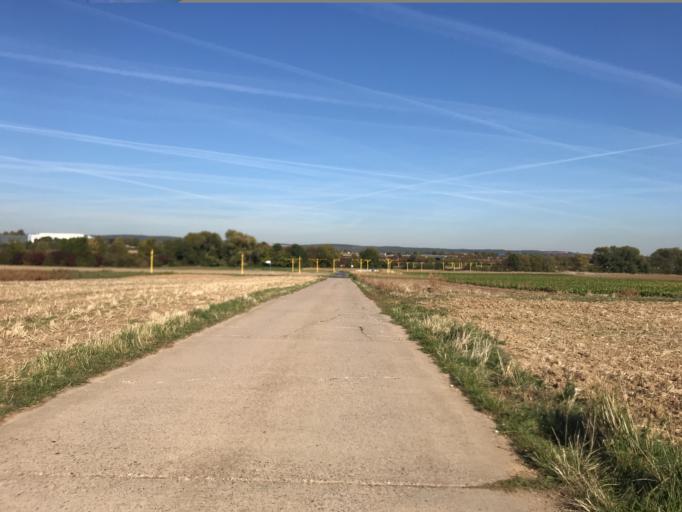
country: DE
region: Hesse
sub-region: Regierungsbezirk Darmstadt
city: Hochheim am Main
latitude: 50.0526
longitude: 8.3433
